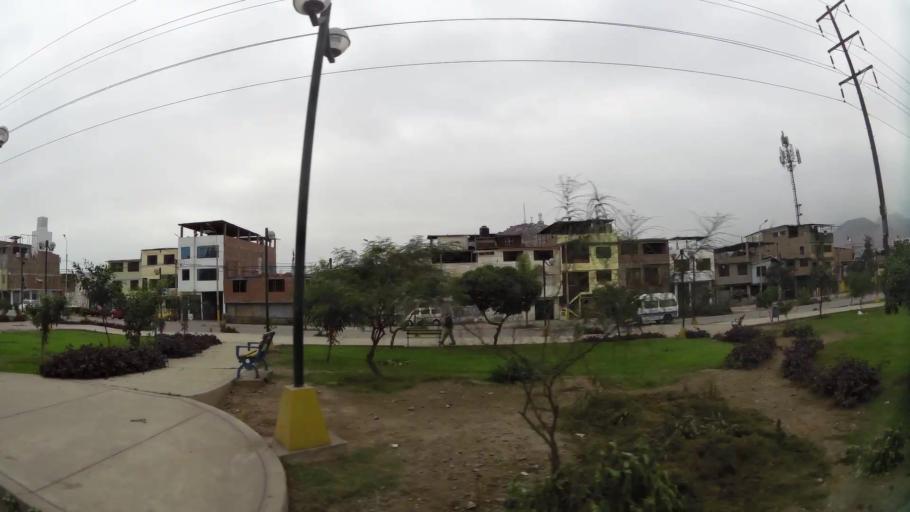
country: PE
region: Lima
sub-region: Lima
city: Surco
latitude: -12.1936
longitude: -76.9495
